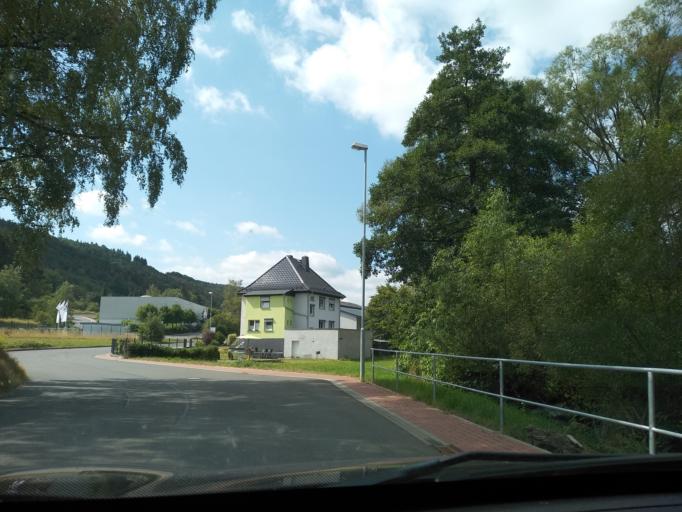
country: DE
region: Hesse
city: Dillenburg
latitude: 50.7877
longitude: 8.3271
